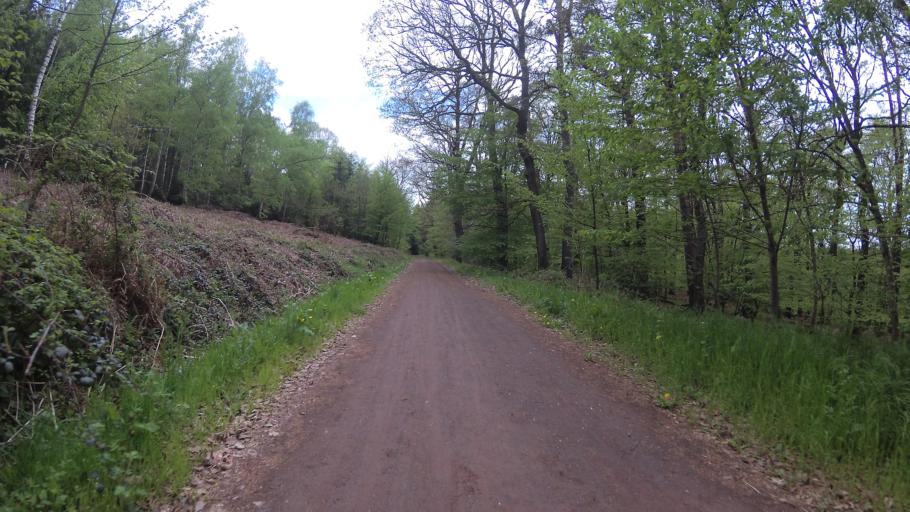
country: DE
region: Saarland
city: Schmelz
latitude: 49.4192
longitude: 6.8584
